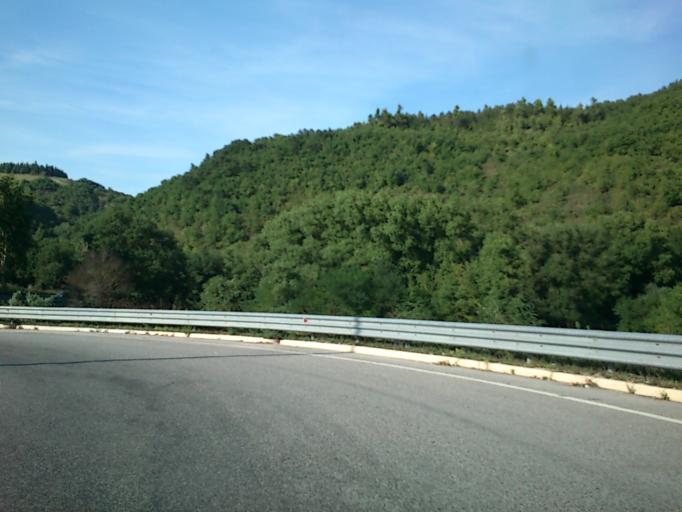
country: IT
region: The Marches
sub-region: Provincia di Pesaro e Urbino
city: Fermignano
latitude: 43.6997
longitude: 12.6637
